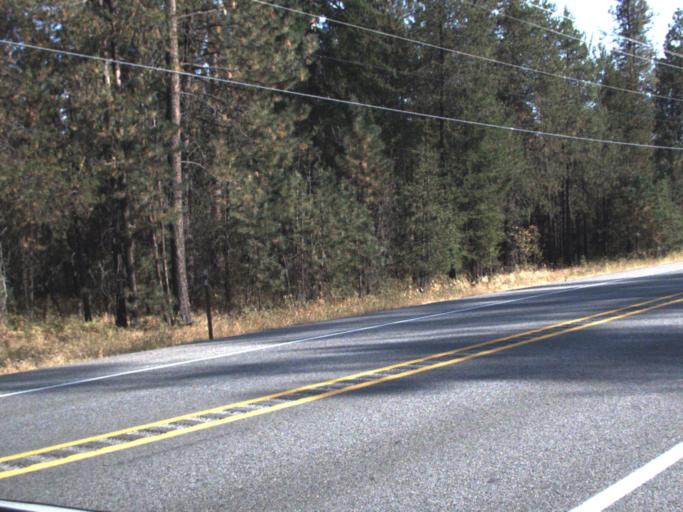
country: US
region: Washington
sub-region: Spokane County
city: Deer Park
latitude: 47.9904
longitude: -117.3496
